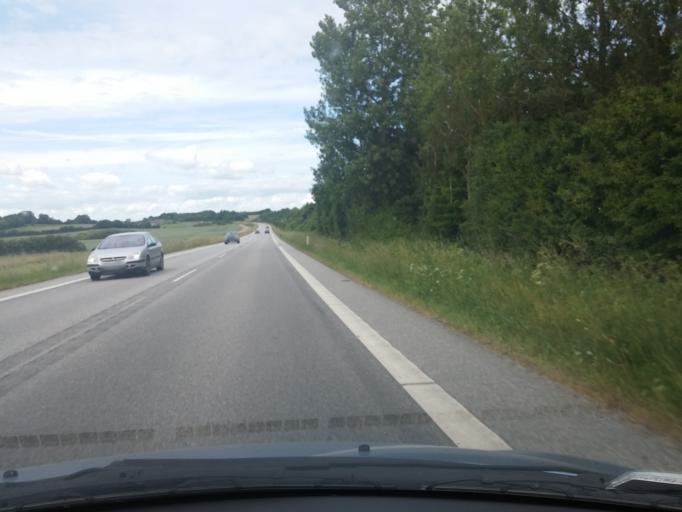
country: DK
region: South Denmark
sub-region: Haderslev Kommune
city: Haderslev
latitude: 55.2744
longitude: 9.4658
